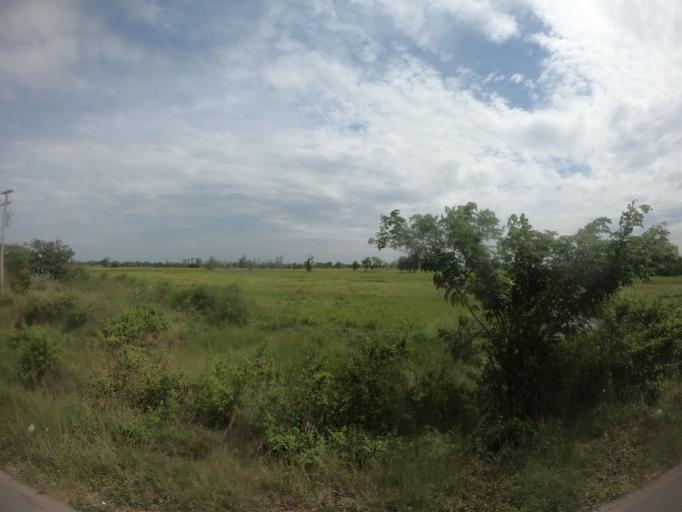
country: TH
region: Maha Sarakham
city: Chiang Yuen
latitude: 16.3727
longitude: 103.1056
